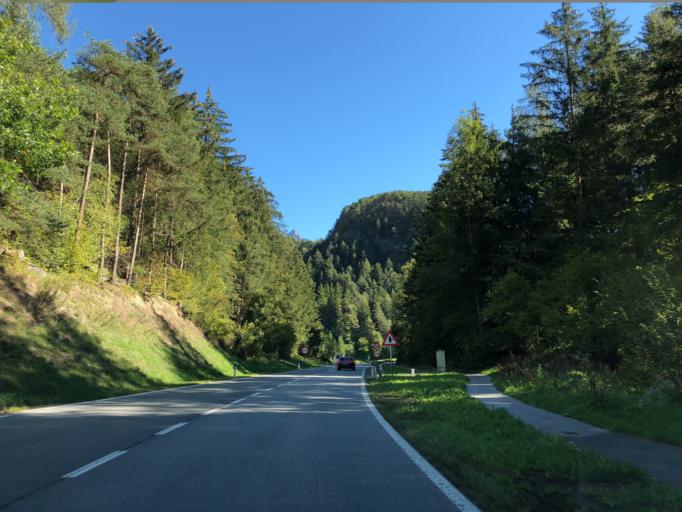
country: AT
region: Tyrol
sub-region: Politischer Bezirk Imst
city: Sautens
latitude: 47.2190
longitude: 10.8648
